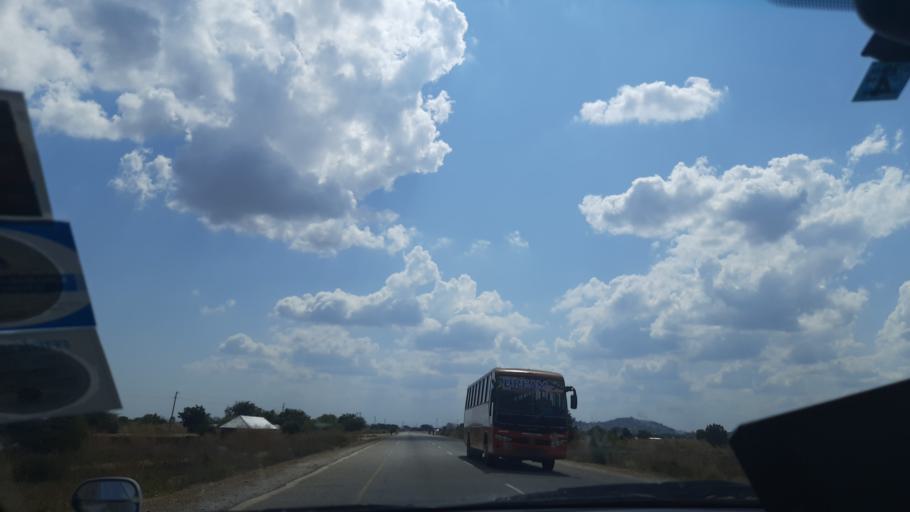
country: TZ
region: Singida
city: Kintinku
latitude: -5.9656
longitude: 35.3306
